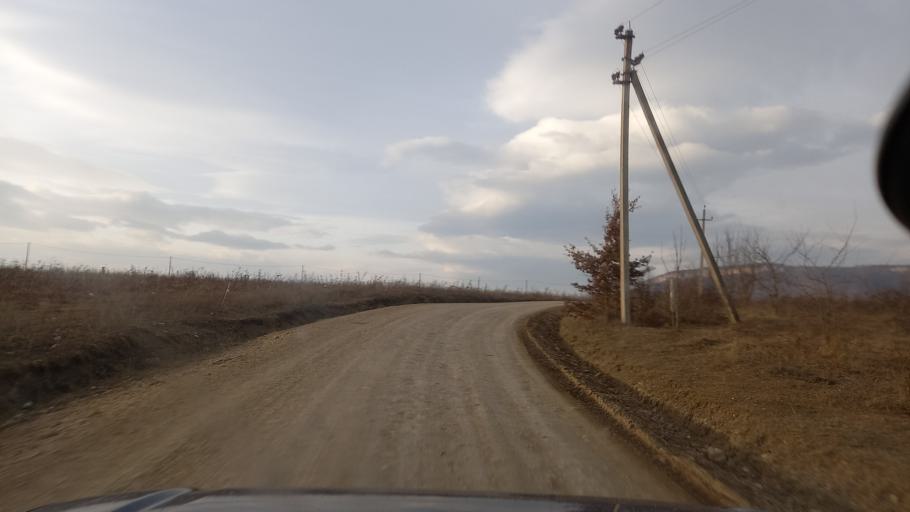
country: RU
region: Adygeya
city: Kamennomostskiy
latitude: 44.1960
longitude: 40.2529
